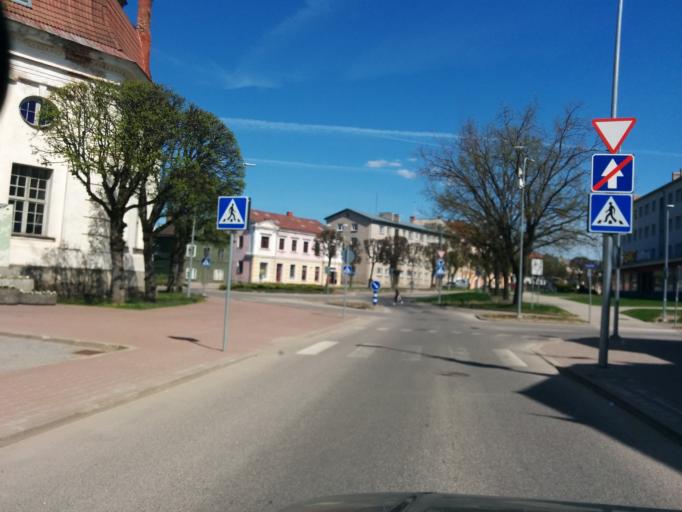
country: EE
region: Valgamaa
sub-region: Valga linn
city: Valga
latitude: 57.7765
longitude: 26.0309
